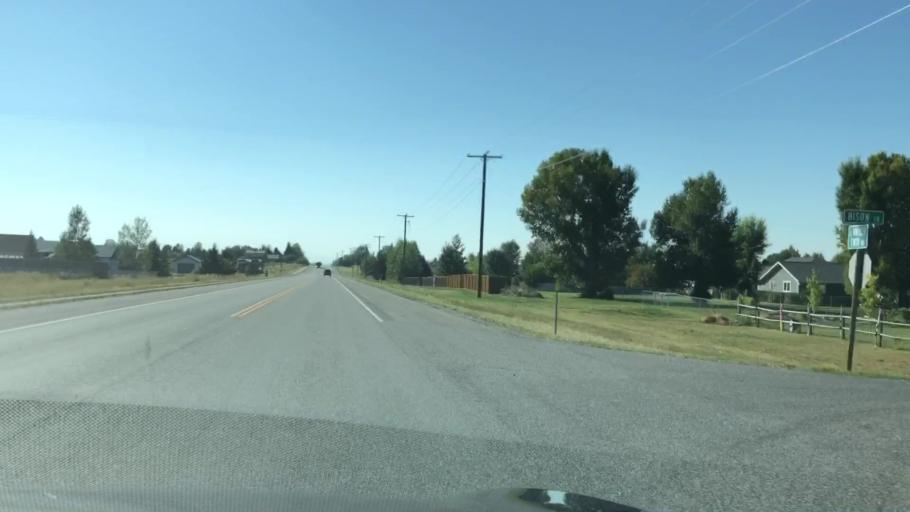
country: US
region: Montana
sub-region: Gallatin County
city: Belgrade
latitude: 45.7293
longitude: -111.1282
